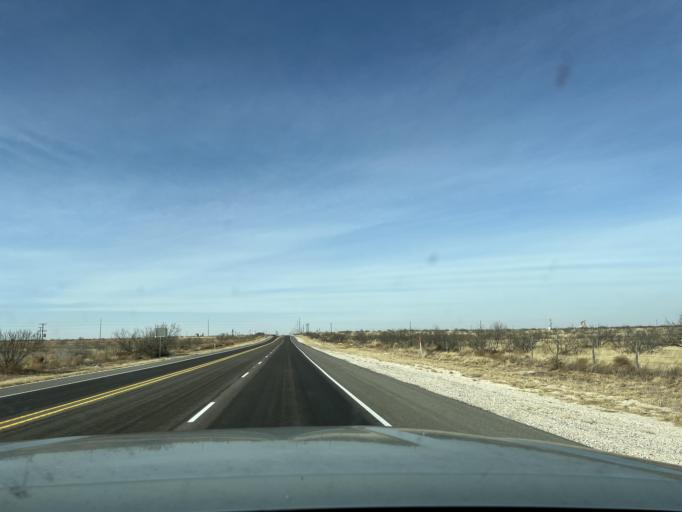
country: US
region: Texas
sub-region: Andrews County
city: Andrews
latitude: 32.3319
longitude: -102.6484
